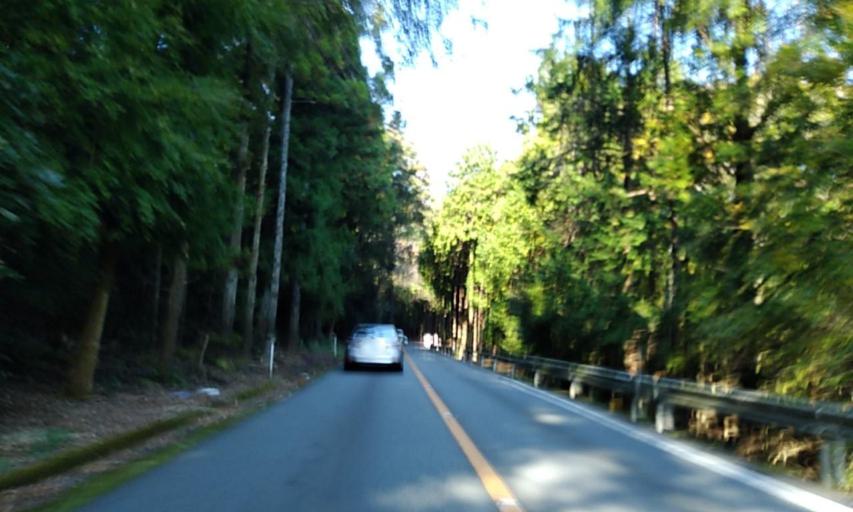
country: JP
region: Mie
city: Ise
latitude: 34.4453
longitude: 136.7519
